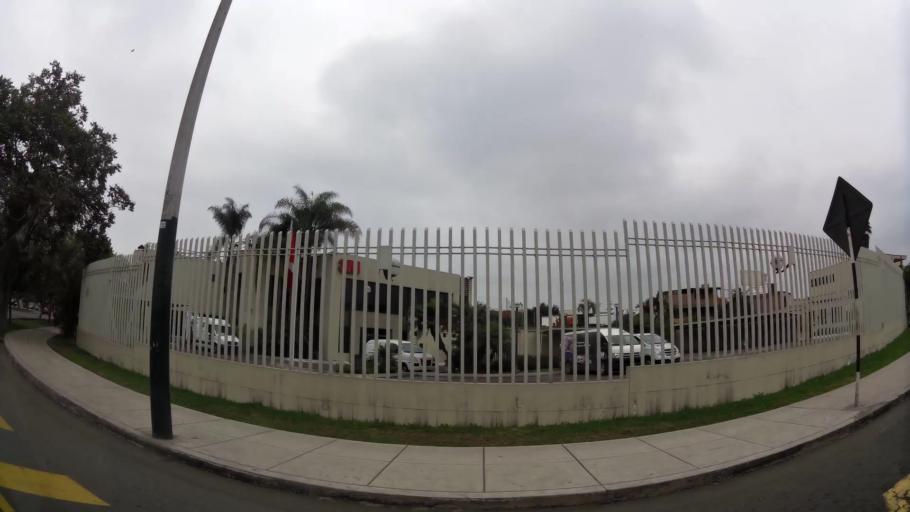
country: PE
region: Lima
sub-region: Lima
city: San Luis
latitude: -12.0977
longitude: -77.0173
